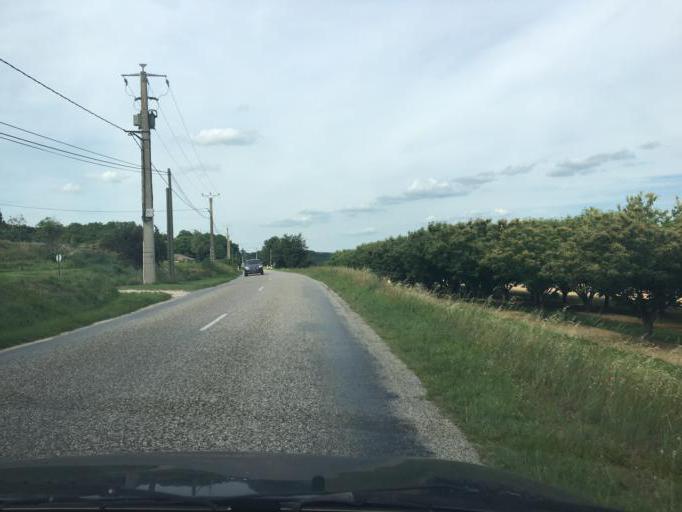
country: FR
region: Rhone-Alpes
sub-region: Departement de la Drome
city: Clerieux
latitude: 45.1004
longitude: 4.9471
